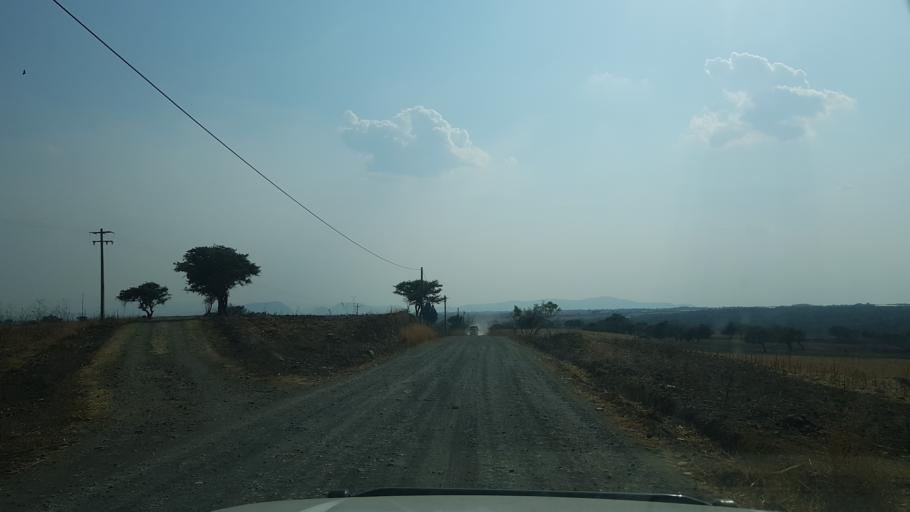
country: MX
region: Morelos
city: Tlacotepec
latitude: 18.7783
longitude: -98.7275
